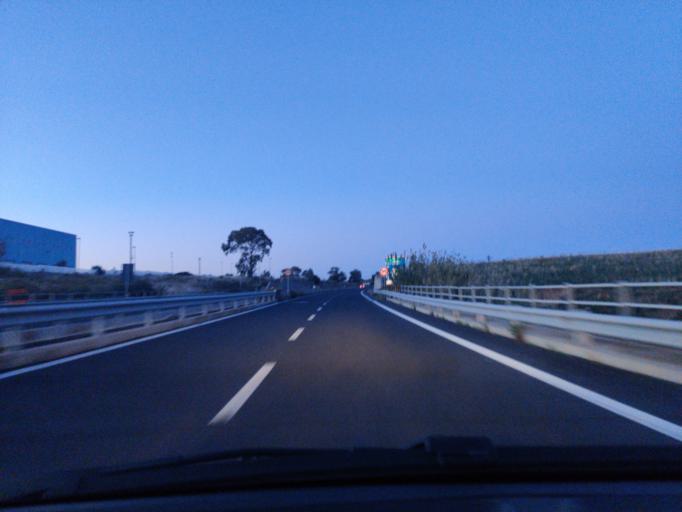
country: IT
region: Latium
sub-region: Citta metropolitana di Roma Capitale
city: Aurelia
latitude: 42.1224
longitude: 11.7910
